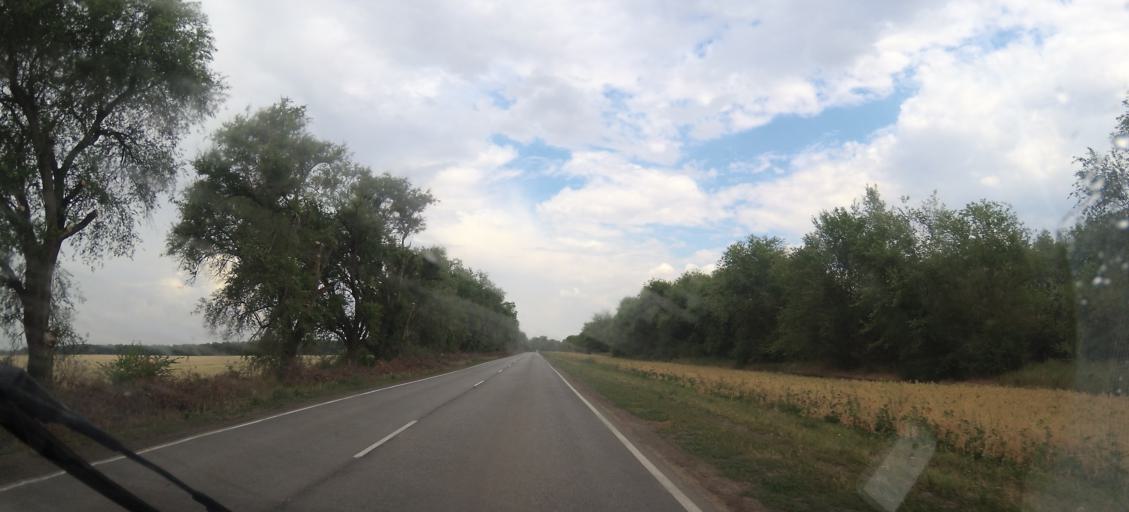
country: RU
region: Rostov
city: Peschanokopskoye
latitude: 46.2026
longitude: 41.1951
